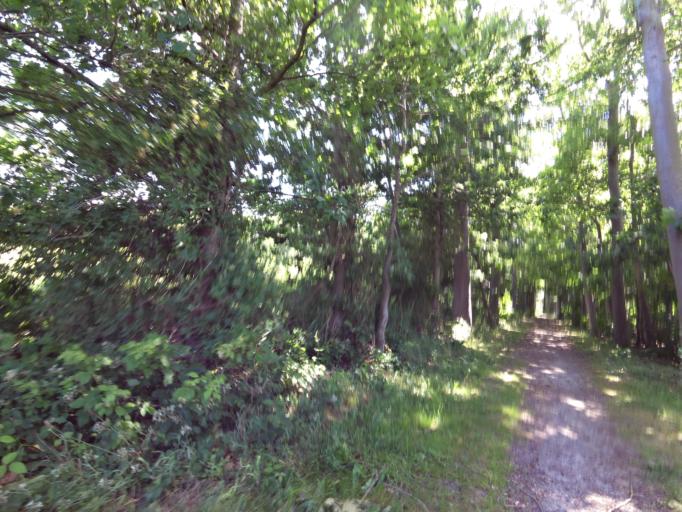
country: BE
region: Flanders
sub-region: Provincie West-Vlaanderen
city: Zedelgem
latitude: 51.1554
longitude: 3.1143
